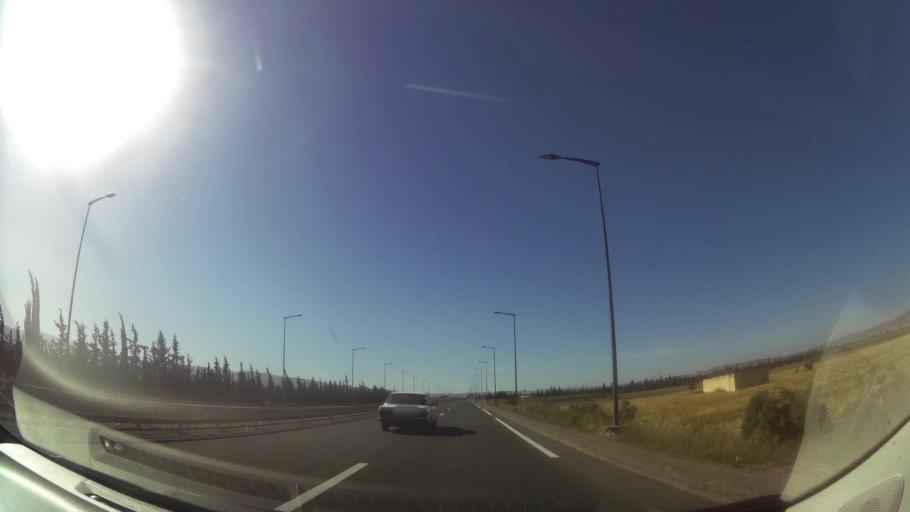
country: MA
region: Oriental
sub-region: Oujda-Angad
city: Oujda
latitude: 34.8189
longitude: -1.9666
